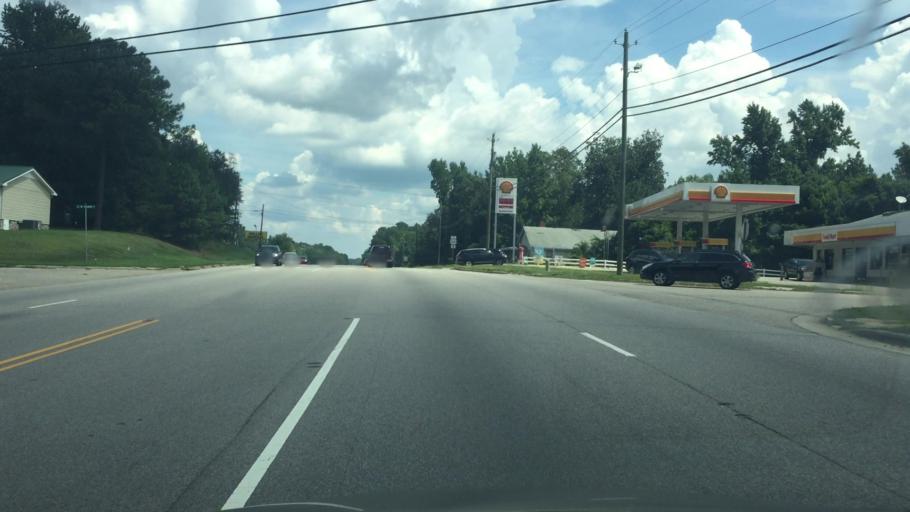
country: US
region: North Carolina
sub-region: Richmond County
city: East Rockingham
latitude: 34.9178
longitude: -79.7850
